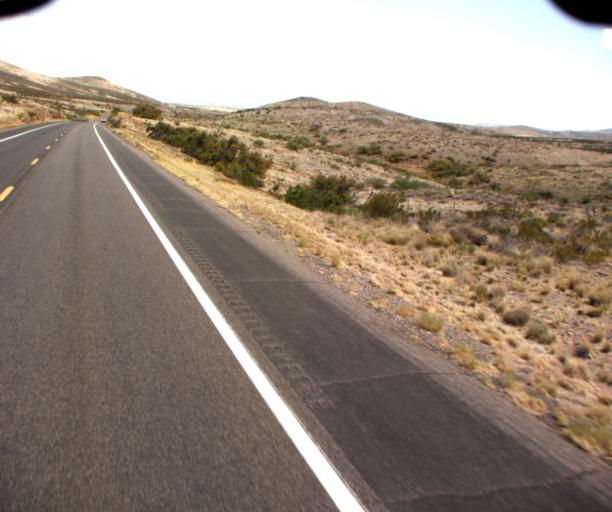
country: US
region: Arizona
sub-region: Greenlee County
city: Clifton
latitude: 32.7429
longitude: -109.2114
